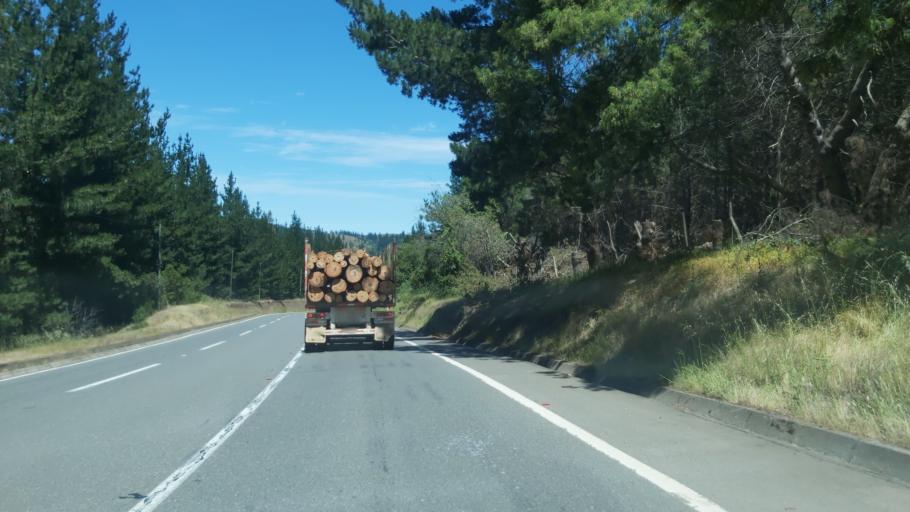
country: CL
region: Maule
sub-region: Provincia de Talca
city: Constitucion
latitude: -35.1517
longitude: -72.2189
